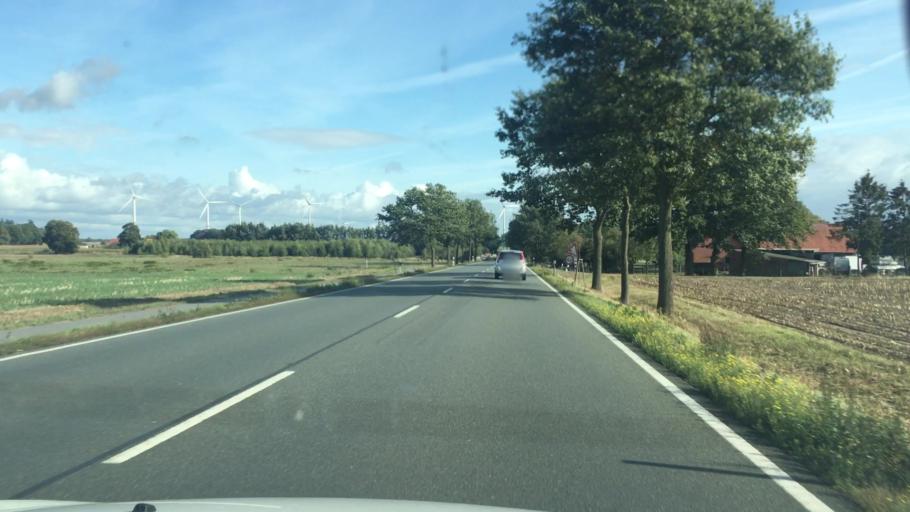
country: DE
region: Lower Saxony
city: Siedenburg
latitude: 52.6757
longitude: 8.9137
